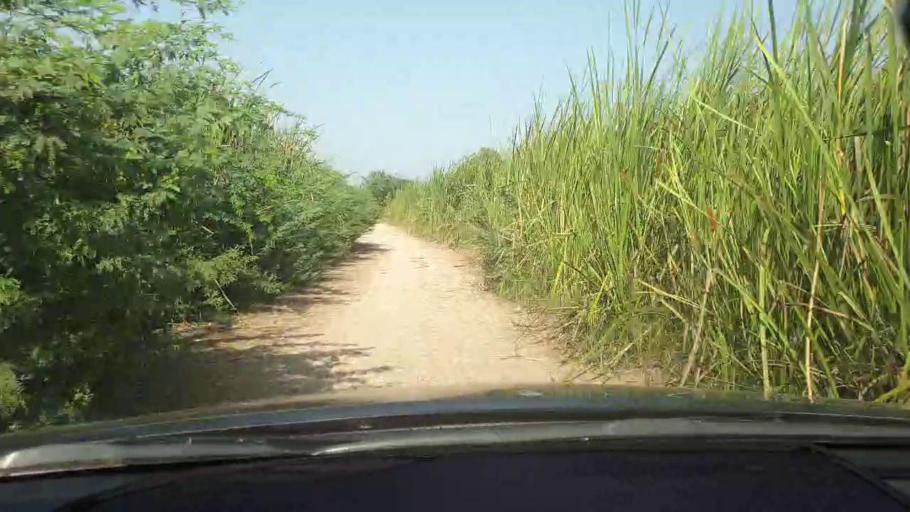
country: PK
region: Sindh
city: Tando Bago
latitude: 24.6833
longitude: 69.0824
